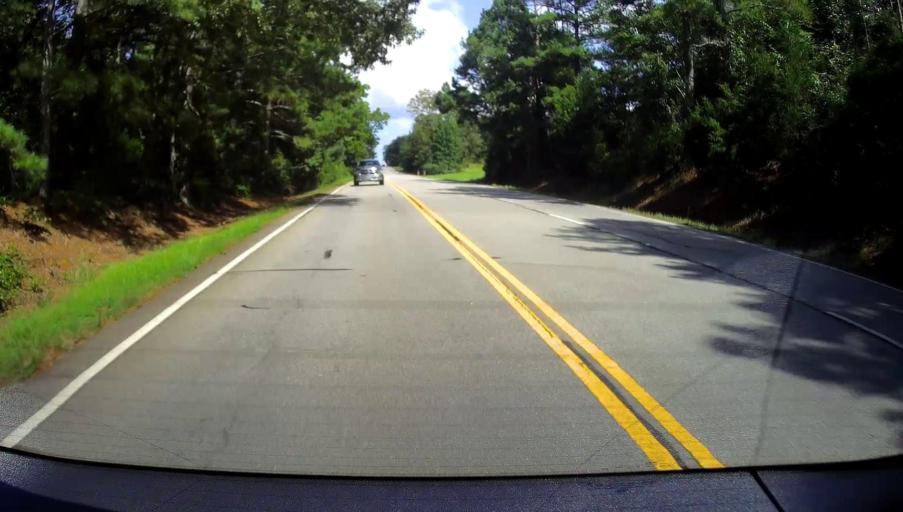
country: US
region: Georgia
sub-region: Upson County
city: Thomaston
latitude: 32.9215
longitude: -84.2090
